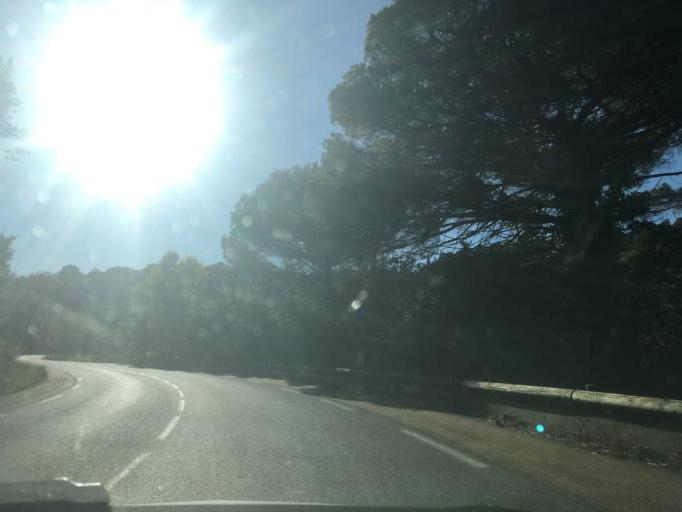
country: FR
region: Provence-Alpes-Cote d'Azur
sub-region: Departement du Var
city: La Garde-Freinet
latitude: 43.3000
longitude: 6.4768
